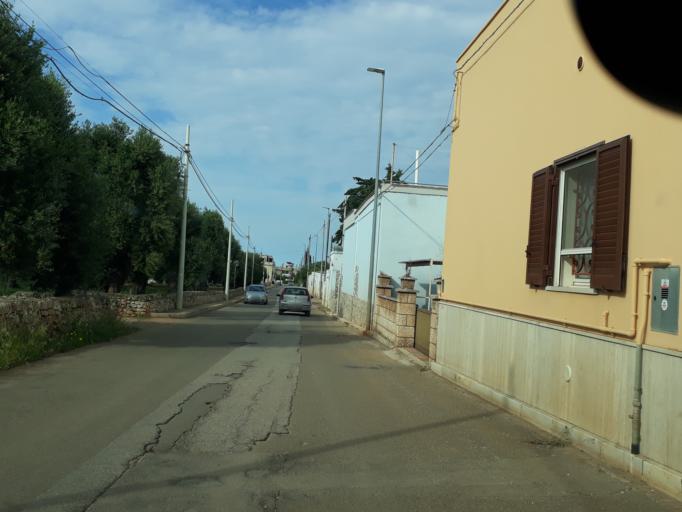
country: IT
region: Apulia
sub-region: Provincia di Brindisi
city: Pezze di Greco
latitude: 40.8070
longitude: 17.4110
